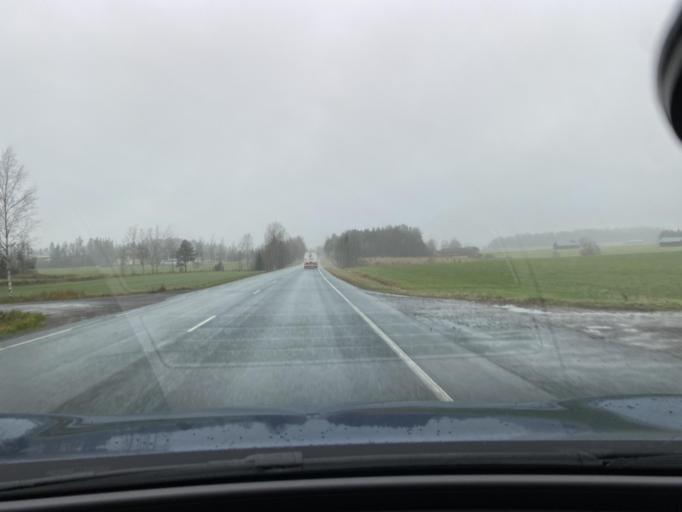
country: FI
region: Haeme
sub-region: Forssa
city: Jokioinen
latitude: 60.7771
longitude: 23.3904
